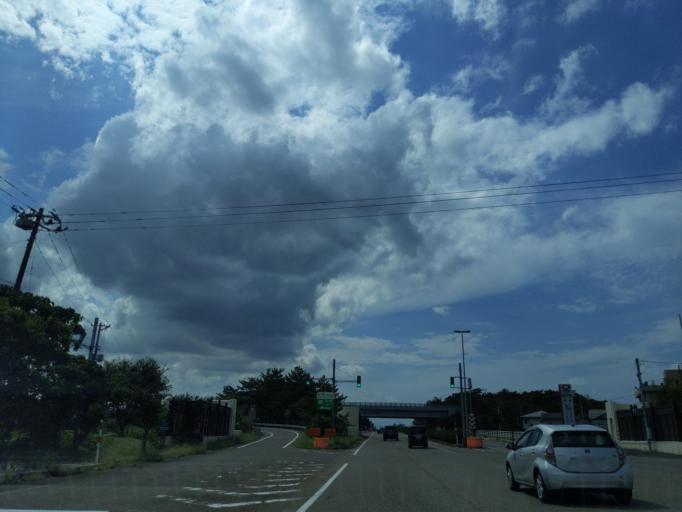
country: JP
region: Niigata
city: Kashiwazaki
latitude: 37.2727
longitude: 138.3913
